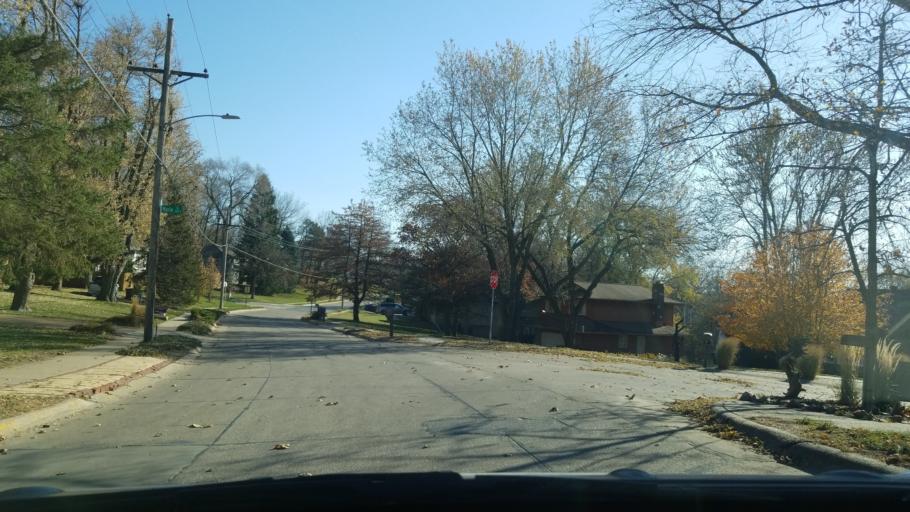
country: US
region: Nebraska
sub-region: Sarpy County
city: Bellevue
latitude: 41.1585
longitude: -95.9022
